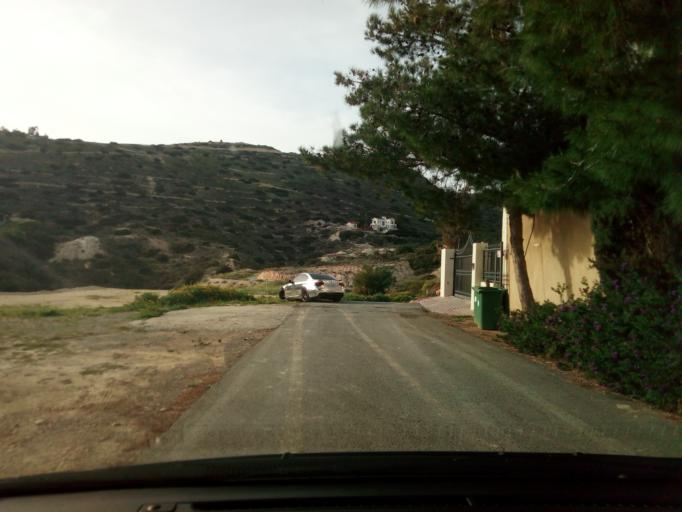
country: CY
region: Larnaka
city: Agios Tychon
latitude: 34.7192
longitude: 33.1286
